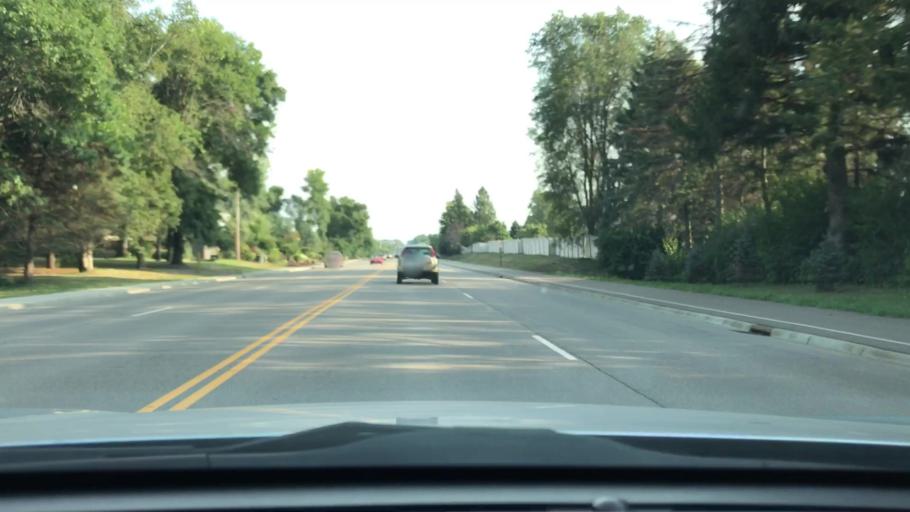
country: US
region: Minnesota
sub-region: Hennepin County
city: Plymouth
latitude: 45.0363
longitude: -93.4818
